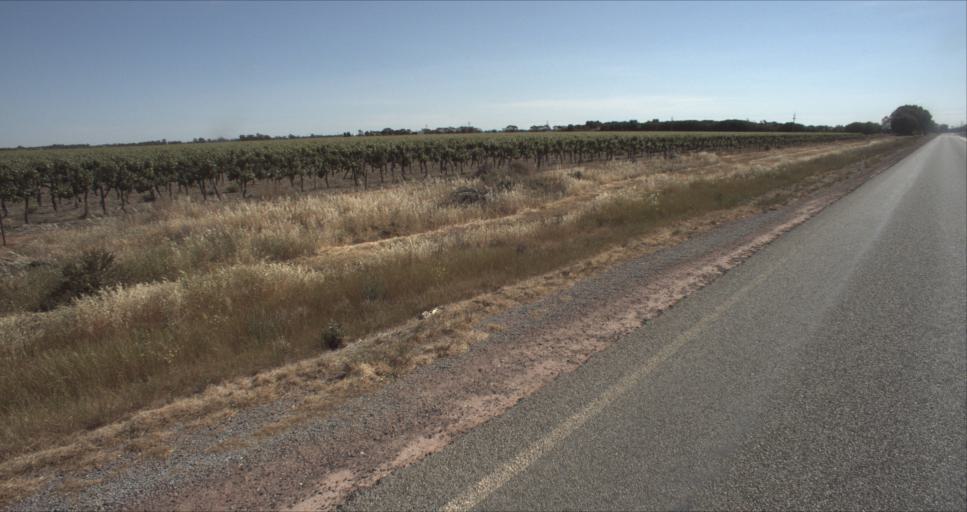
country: AU
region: New South Wales
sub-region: Leeton
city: Leeton
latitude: -34.5015
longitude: 146.4025
